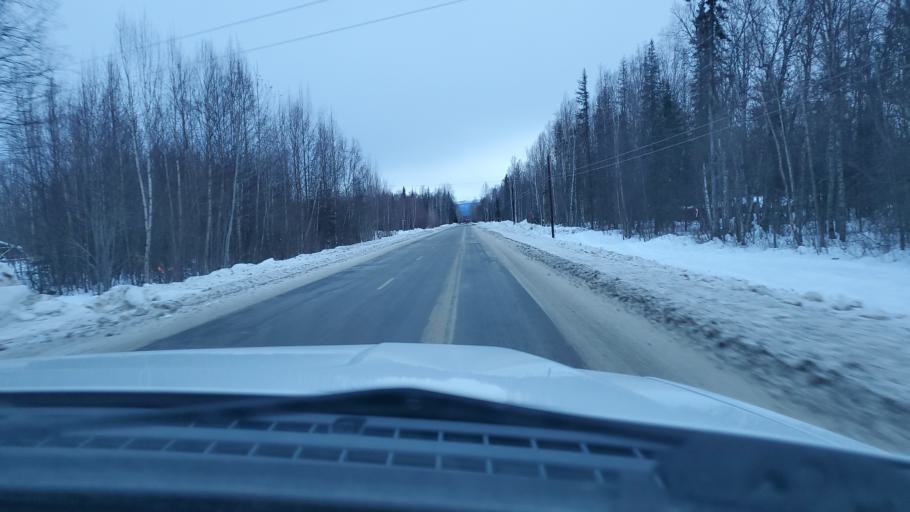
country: US
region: Alaska
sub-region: Matanuska-Susitna Borough
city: Y
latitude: 62.3163
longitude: -150.2568
